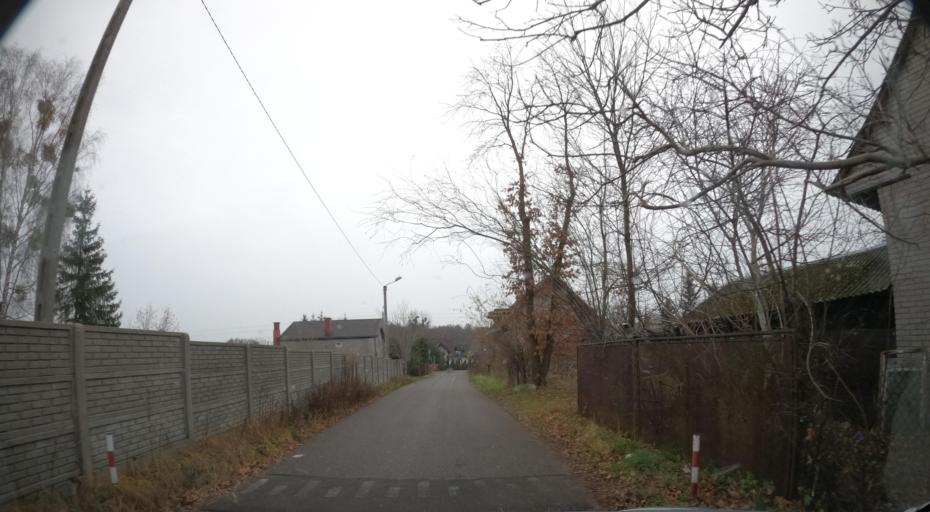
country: PL
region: Masovian Voivodeship
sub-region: Powiat radomski
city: Jastrzebia
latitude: 51.4288
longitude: 21.2318
